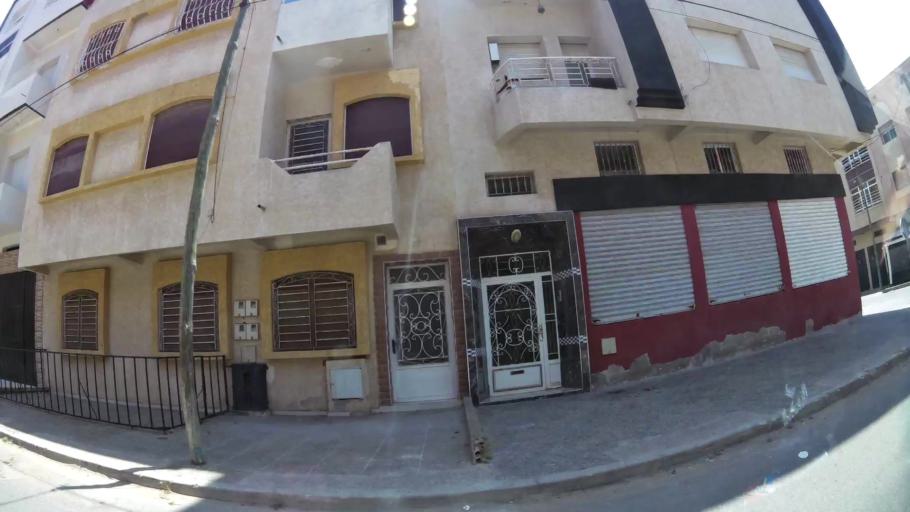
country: MA
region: Gharb-Chrarda-Beni Hssen
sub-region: Kenitra Province
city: Kenitra
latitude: 34.2522
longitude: -6.6120
